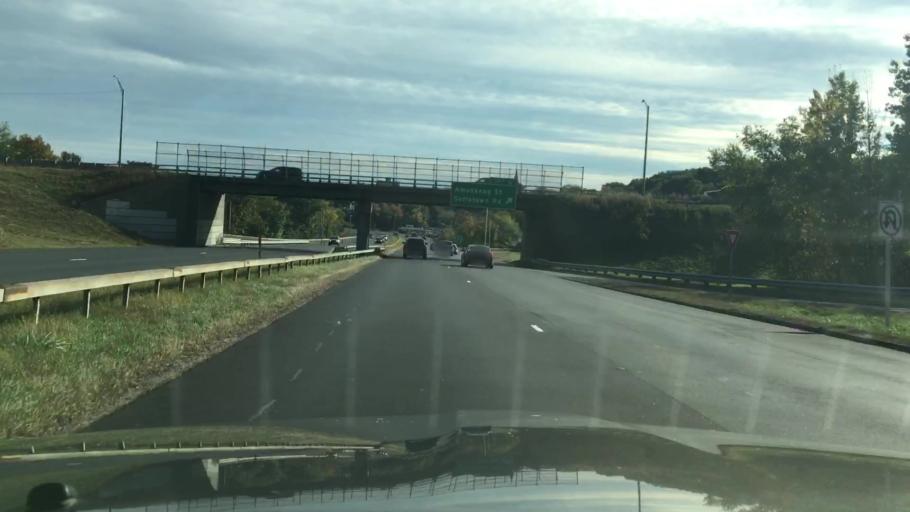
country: US
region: New Hampshire
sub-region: Hillsborough County
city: Manchester
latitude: 43.0032
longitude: -71.4753
